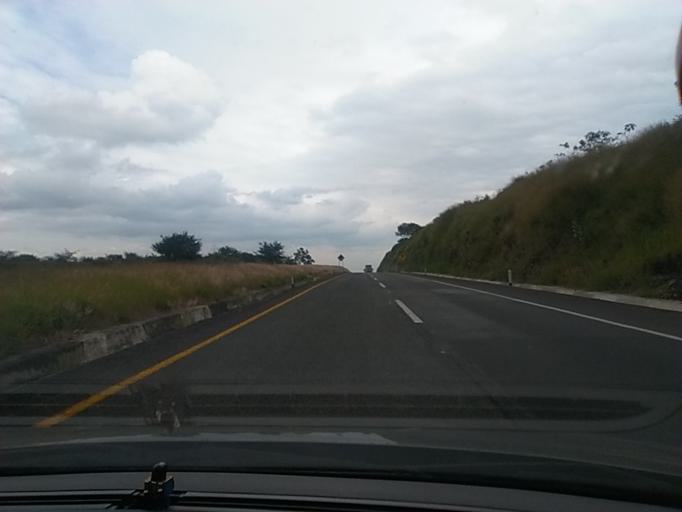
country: MX
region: Jalisco
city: Ocotlan
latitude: 20.4182
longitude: -102.7553
